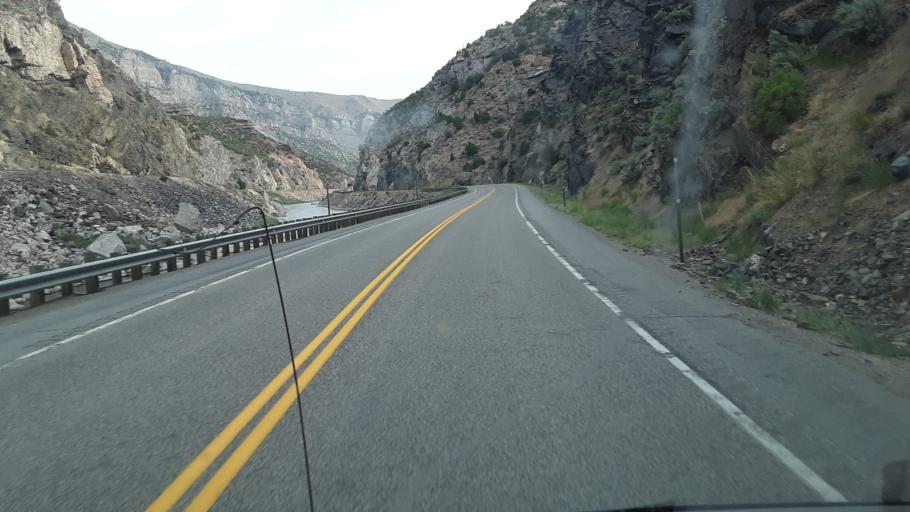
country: US
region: Wyoming
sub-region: Hot Springs County
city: Thermopolis
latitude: 43.4530
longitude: -108.1698
